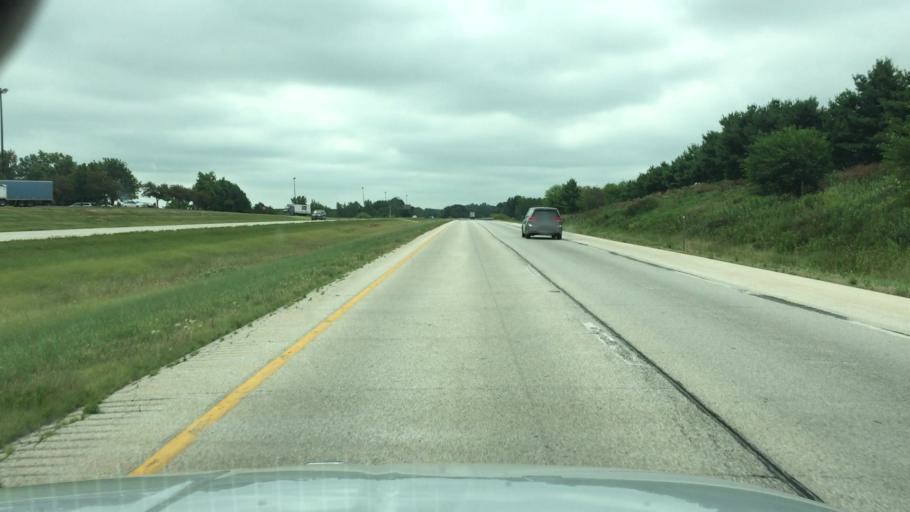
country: US
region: Illinois
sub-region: Henry County
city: Orion
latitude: 41.2156
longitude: -90.3320
